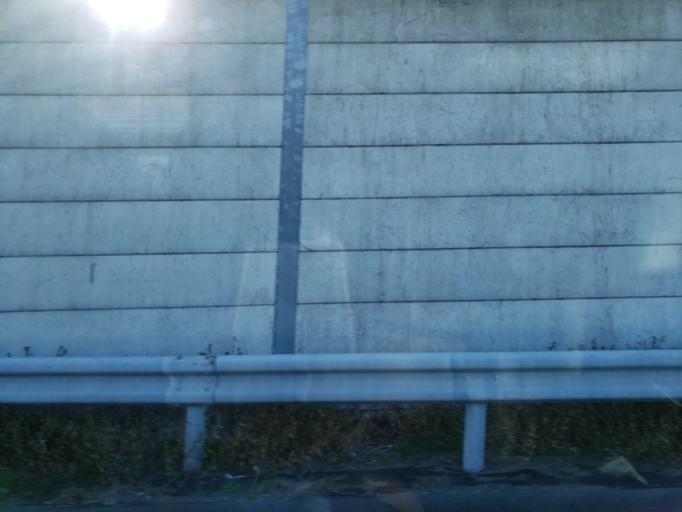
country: JP
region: Hyogo
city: Akashi
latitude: 34.5162
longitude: 134.8809
